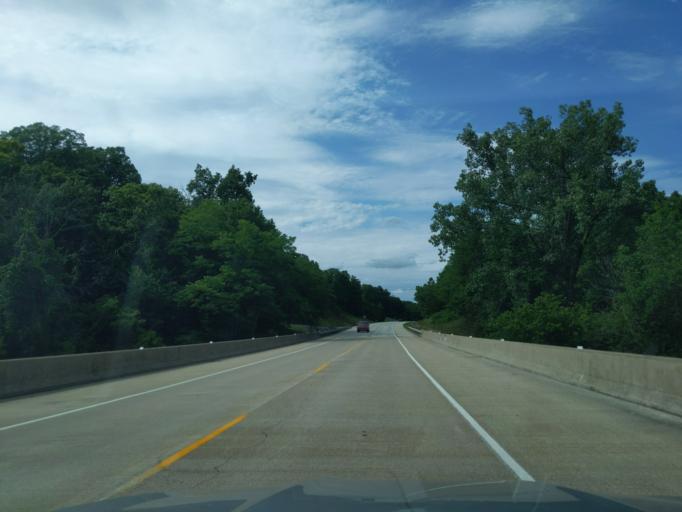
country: US
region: Indiana
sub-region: Ripley County
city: Batesville
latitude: 39.2095
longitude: -85.2088
